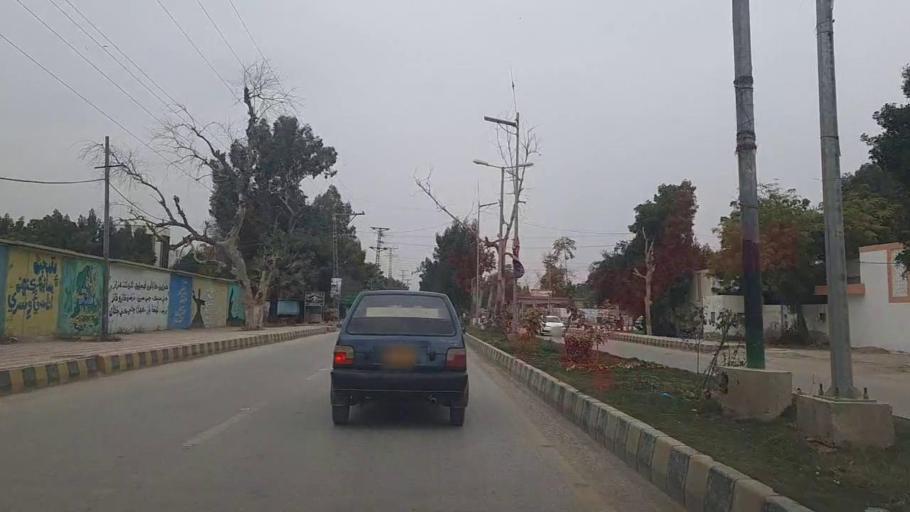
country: PK
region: Sindh
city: Nawabshah
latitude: 26.2466
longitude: 68.4018
